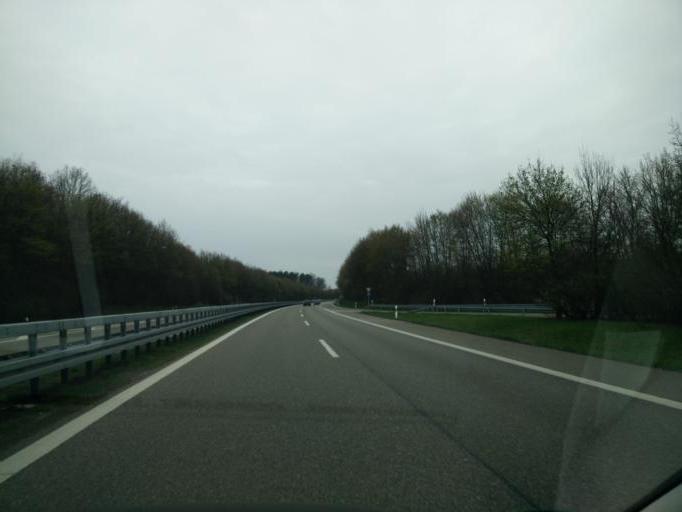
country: DE
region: Baden-Wuerttemberg
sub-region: Regierungsbezirk Stuttgart
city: Filderstadt
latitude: 48.6311
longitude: 9.2264
